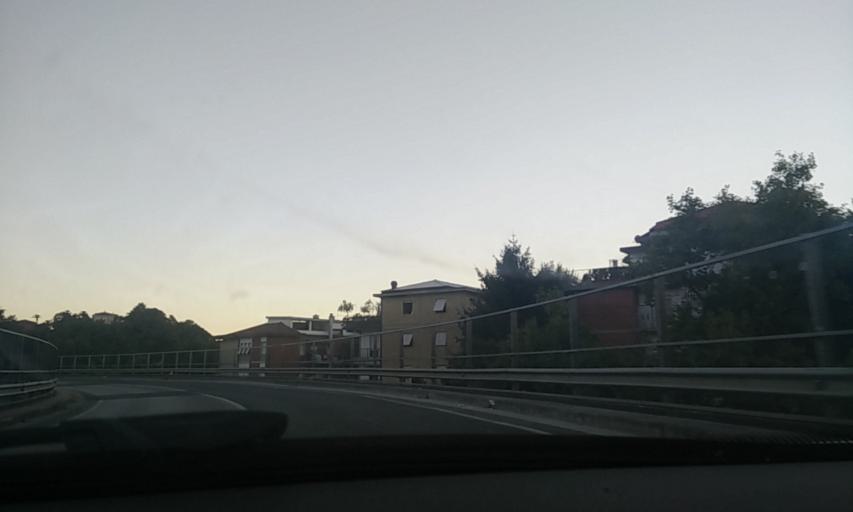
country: IT
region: Tuscany
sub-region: Provincia di Massa-Carrara
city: Carrara
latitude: 44.0713
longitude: 10.0848
